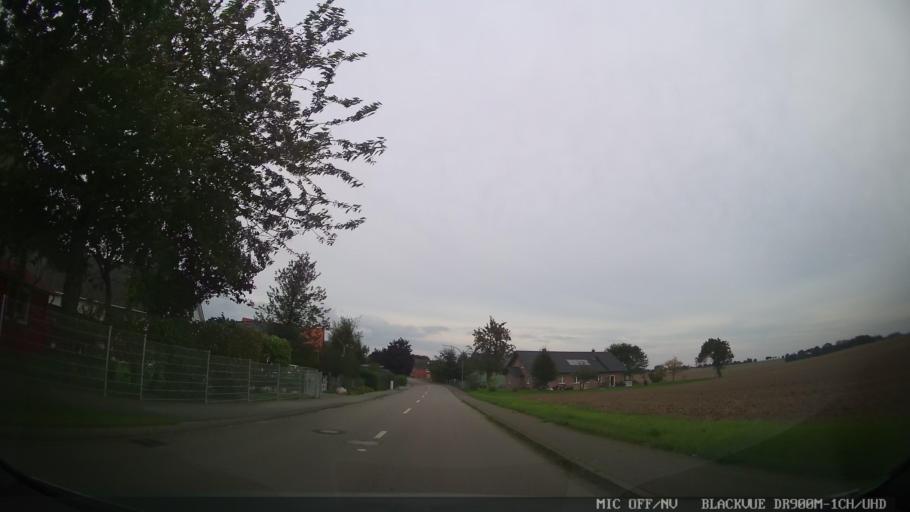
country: DE
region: Schleswig-Holstein
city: Grube
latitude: 54.2734
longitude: 11.0628
